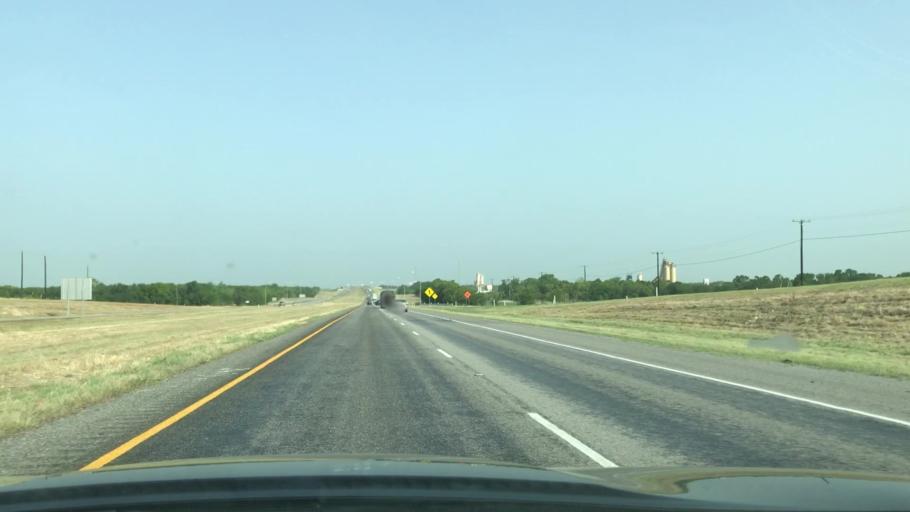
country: US
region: Texas
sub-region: Kaufman County
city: Talty
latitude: 32.7306
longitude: -96.3411
